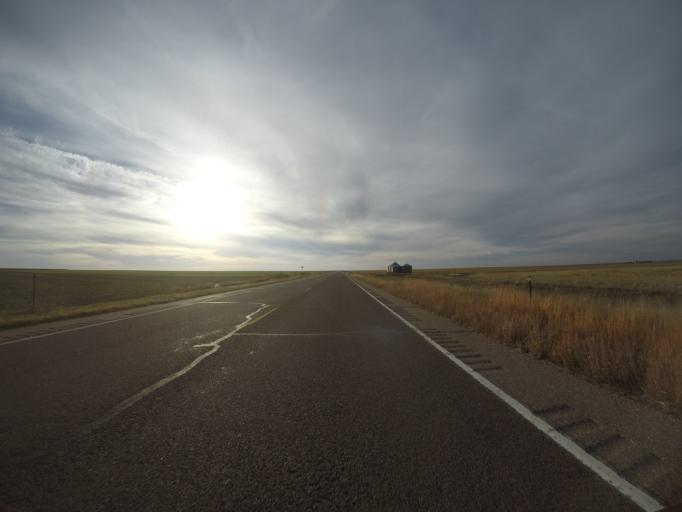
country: US
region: Colorado
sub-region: Kit Carson County
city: Burlington
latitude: 39.6579
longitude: -102.4787
